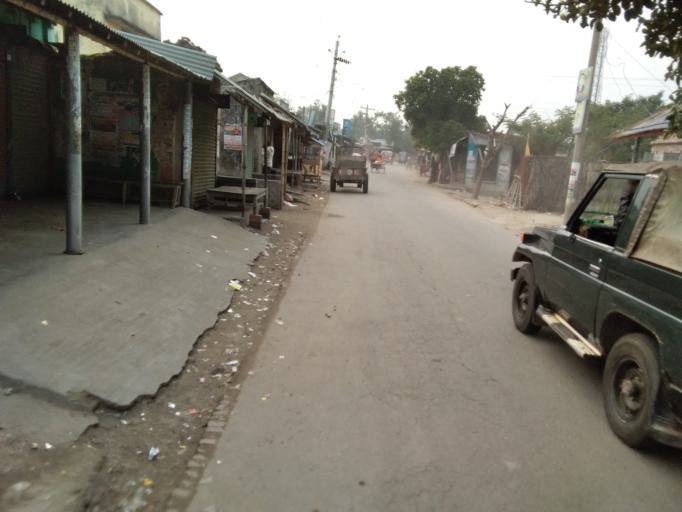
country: BD
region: Khulna
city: Satkhira
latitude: 22.5872
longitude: 89.0633
